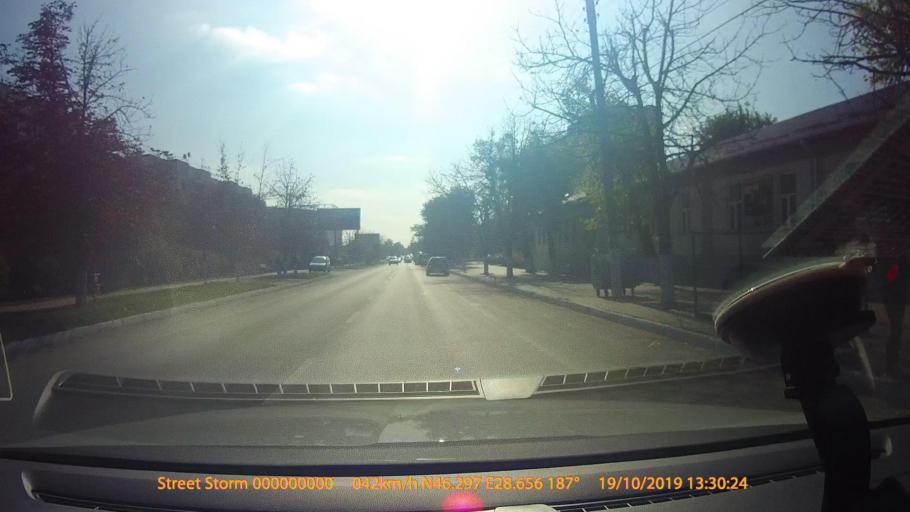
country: MD
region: Gagauzia
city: Comrat
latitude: 46.2969
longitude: 28.6556
